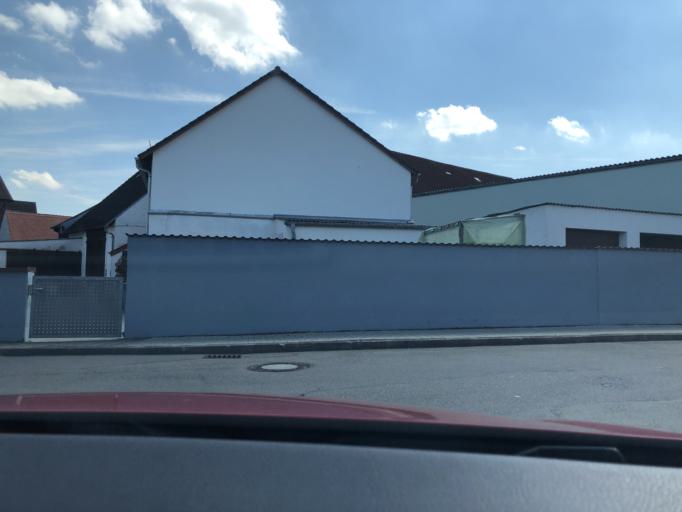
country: DE
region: Bavaria
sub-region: Upper Bavaria
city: Lenting
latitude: 48.7741
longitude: 11.4867
